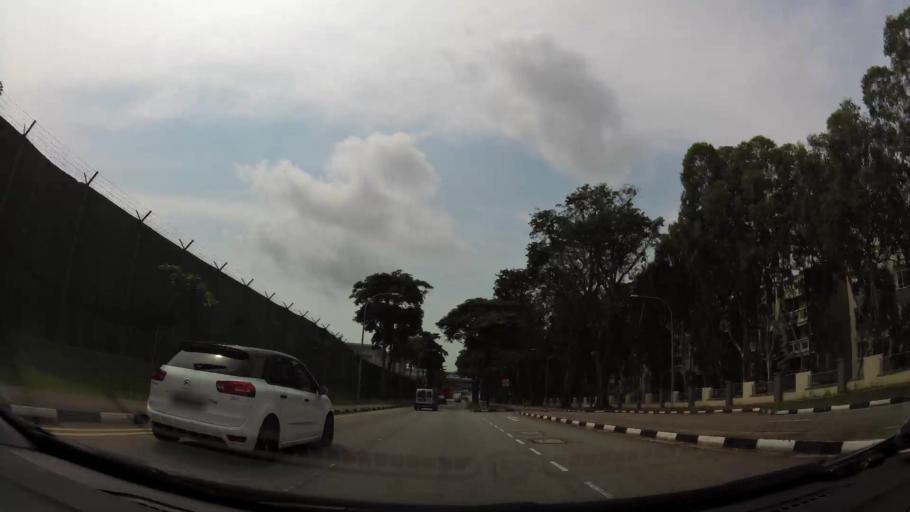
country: SG
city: Singapore
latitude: 1.3568
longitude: 103.9693
